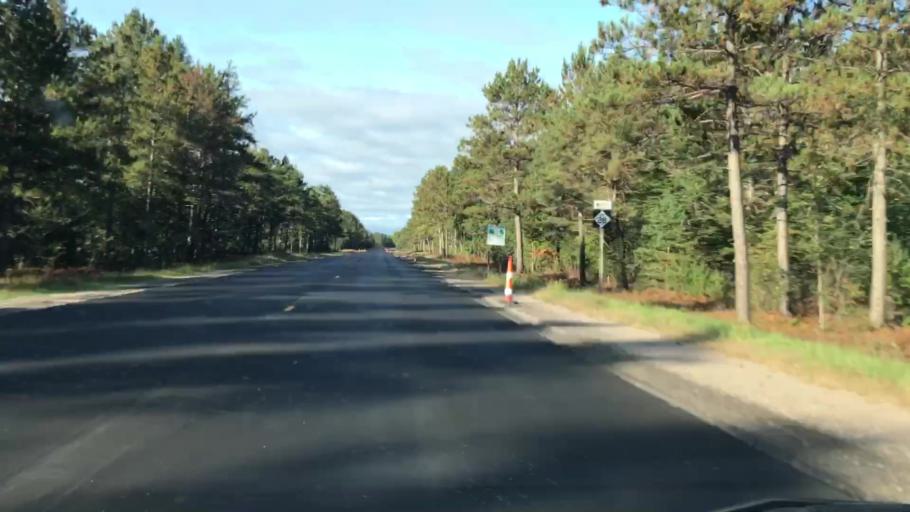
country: US
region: Michigan
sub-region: Mackinac County
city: Saint Ignace
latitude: 46.3515
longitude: -84.9062
